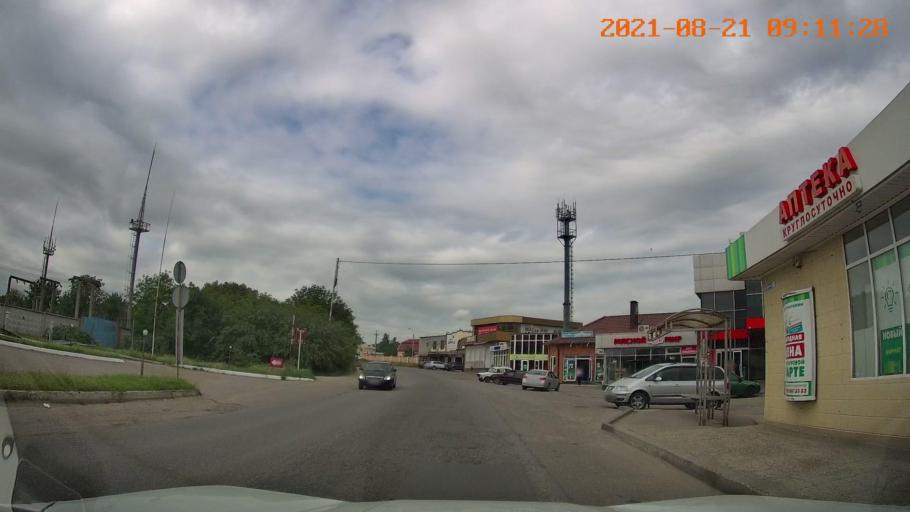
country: RU
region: Stavropol'skiy
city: Svobody
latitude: 44.0179
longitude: 43.0707
